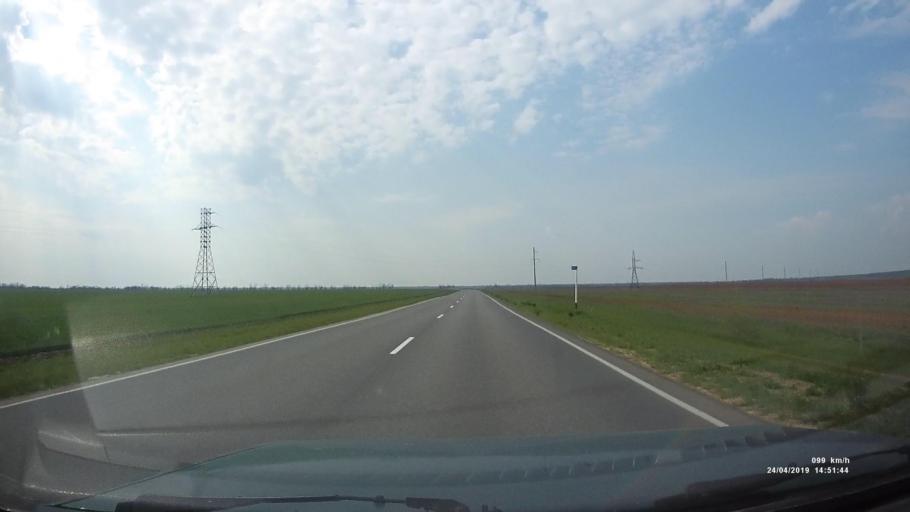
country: RU
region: Rostov
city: Remontnoye
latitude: 46.5271
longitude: 43.6950
